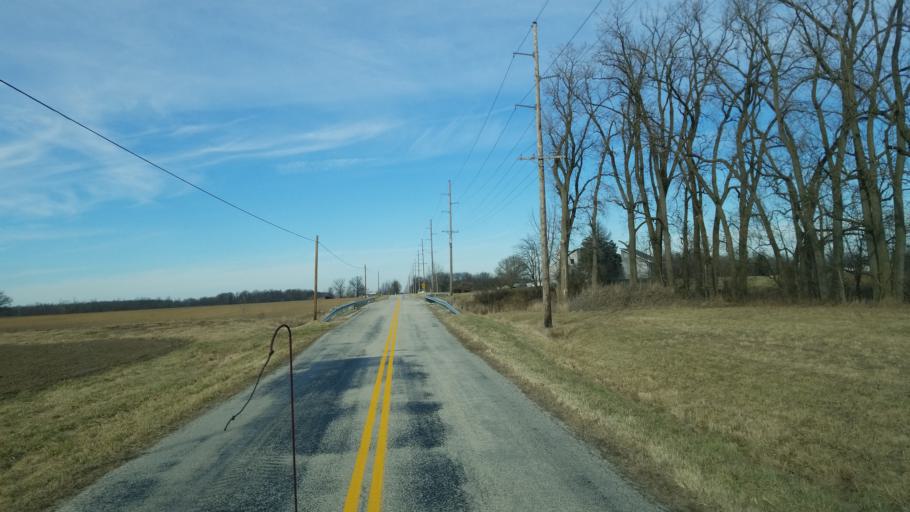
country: US
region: Ohio
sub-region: Wyandot County
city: Upper Sandusky
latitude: 40.6665
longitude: -83.3241
